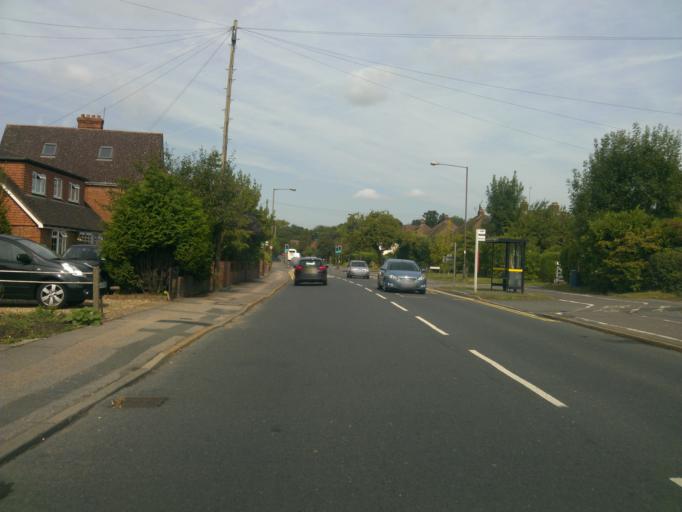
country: GB
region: England
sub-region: Kent
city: Tonbridge
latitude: 51.2082
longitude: 0.2589
